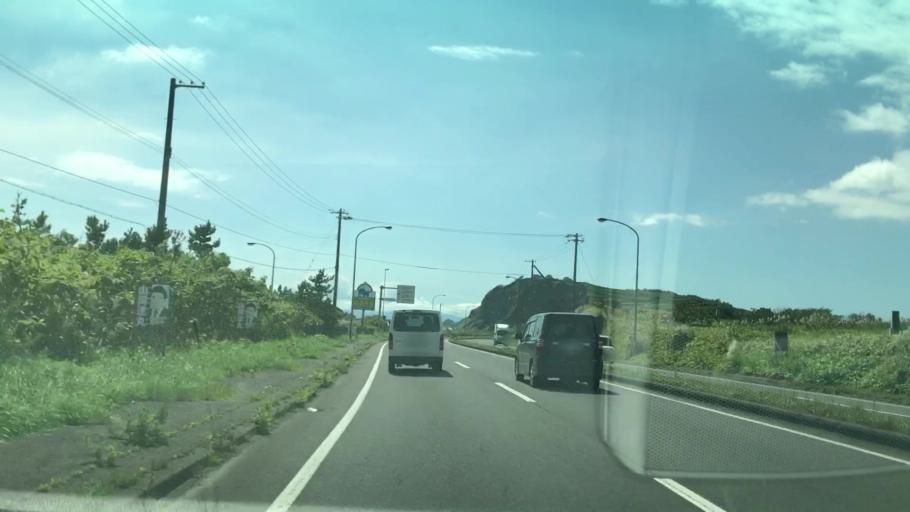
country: JP
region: Hokkaido
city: Muroran
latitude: 42.3473
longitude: 141.0384
